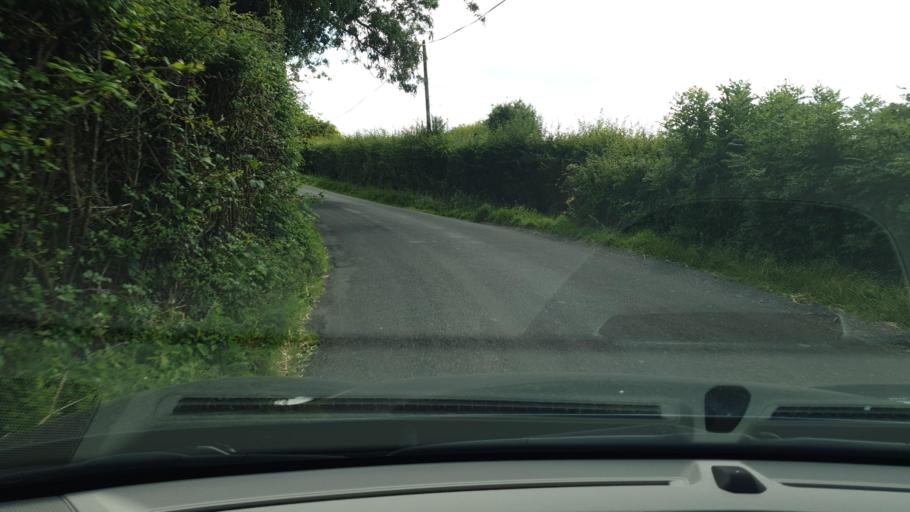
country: IE
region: Leinster
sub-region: An Mhi
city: Dunboyne
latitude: 53.4070
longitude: -6.4916
